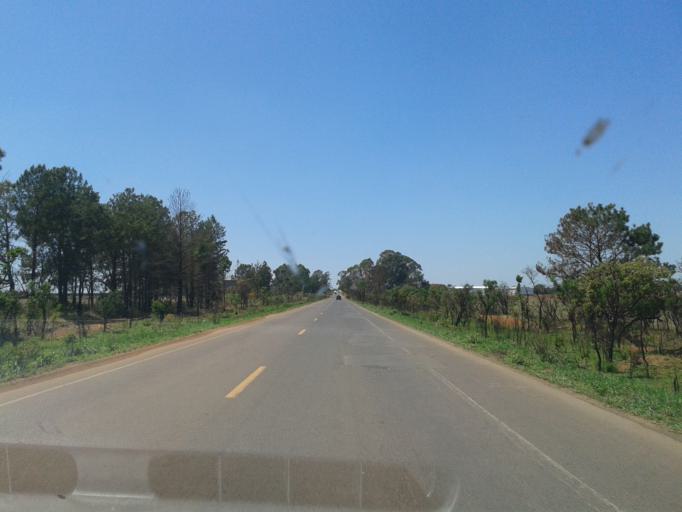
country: BR
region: Minas Gerais
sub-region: Araxa
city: Araxa
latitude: -19.4080
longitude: -47.3104
